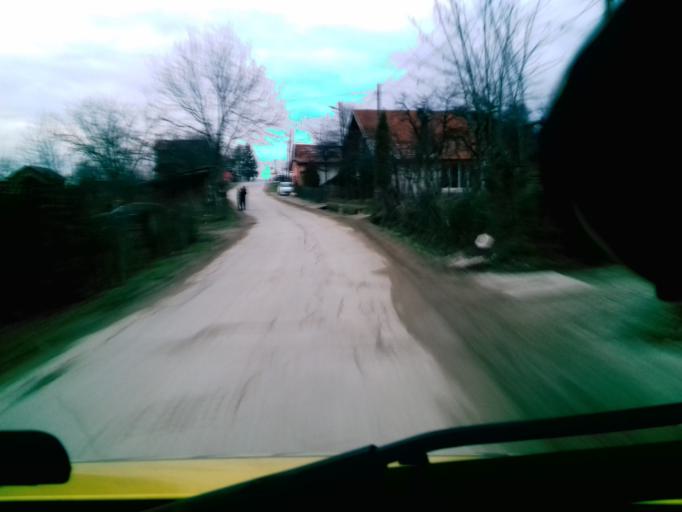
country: BA
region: Federation of Bosnia and Herzegovina
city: Zenica
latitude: 44.1839
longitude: 17.9693
